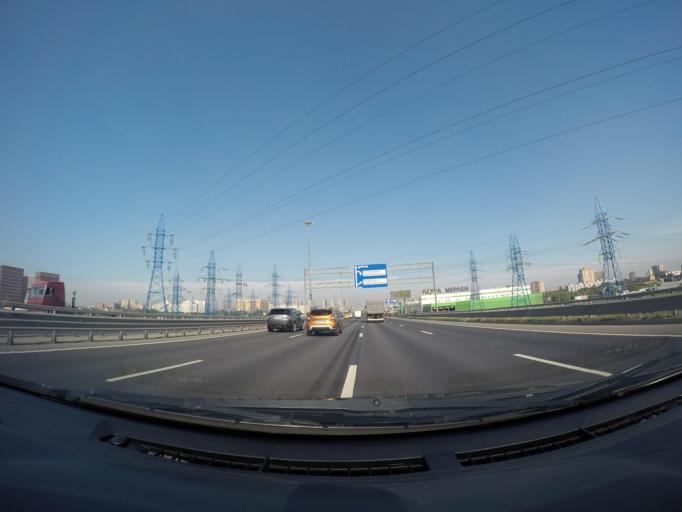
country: RU
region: Moskovskaya
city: Lyubertsy
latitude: 55.6622
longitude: 37.8865
